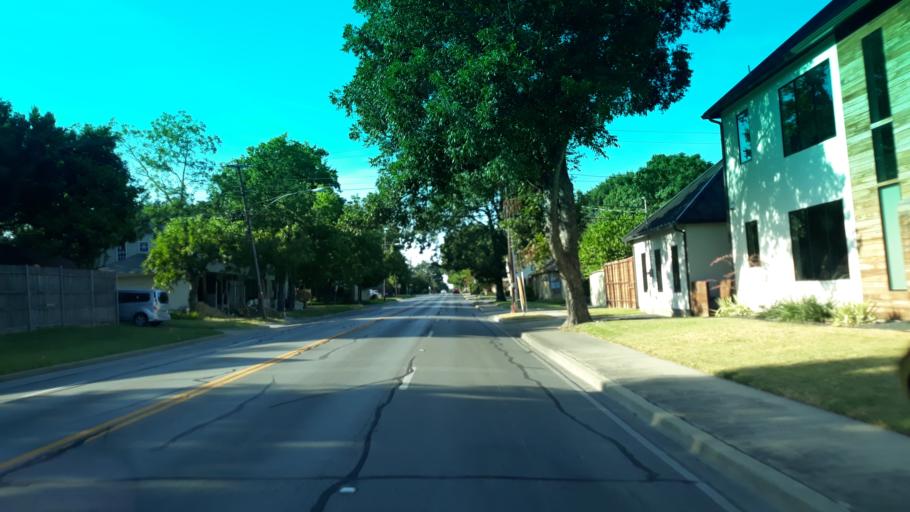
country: US
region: Texas
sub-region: Dallas County
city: Highland Park
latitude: 32.8280
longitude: -96.7615
